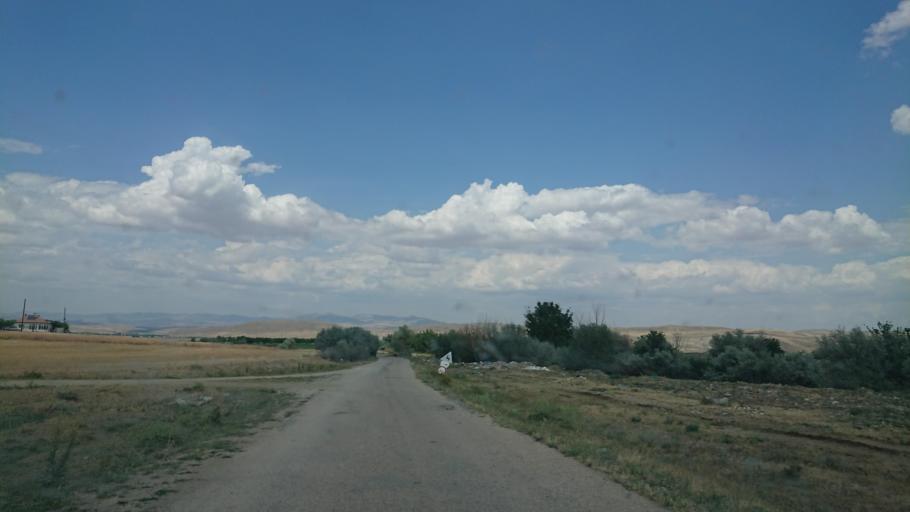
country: TR
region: Aksaray
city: Sariyahsi
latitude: 38.9662
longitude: 33.8904
